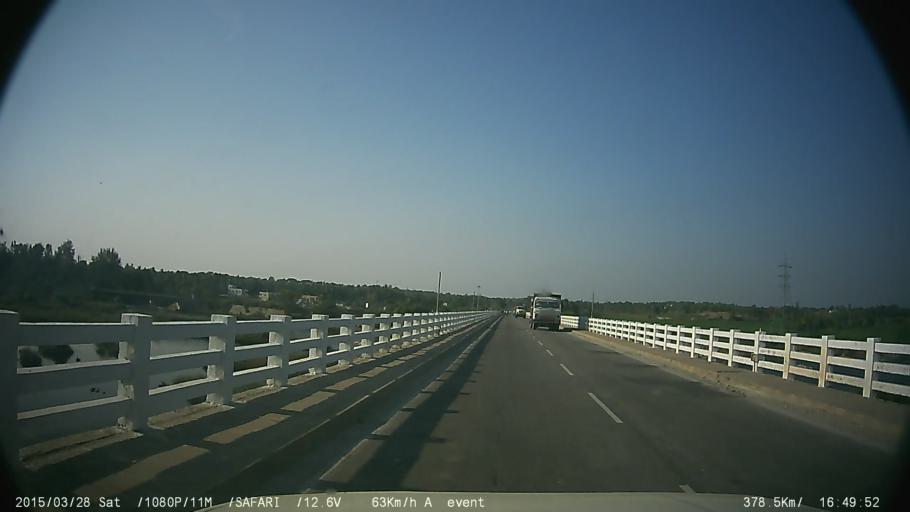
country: IN
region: Karnataka
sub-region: Mandya
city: Shrirangapattana
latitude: 12.4230
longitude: 76.5813
